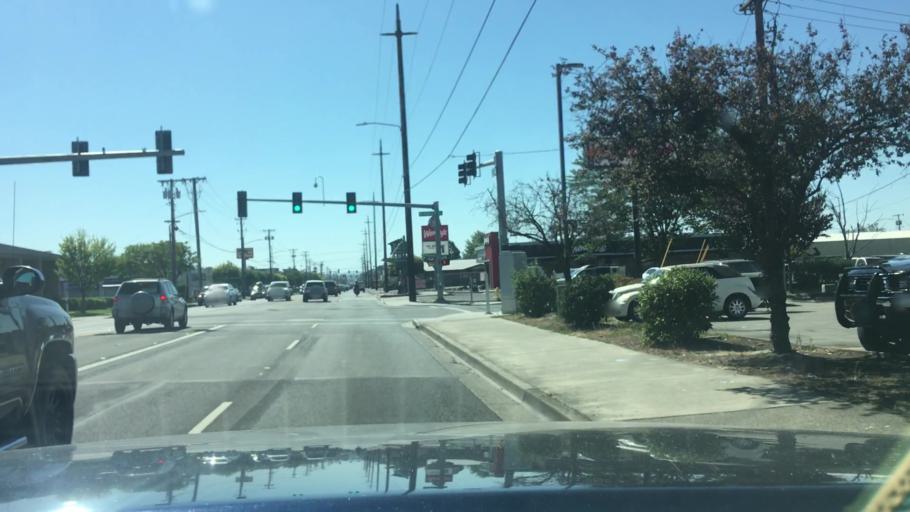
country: US
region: Oregon
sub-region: Lane County
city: Eugene
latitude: 44.0479
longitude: -123.1294
